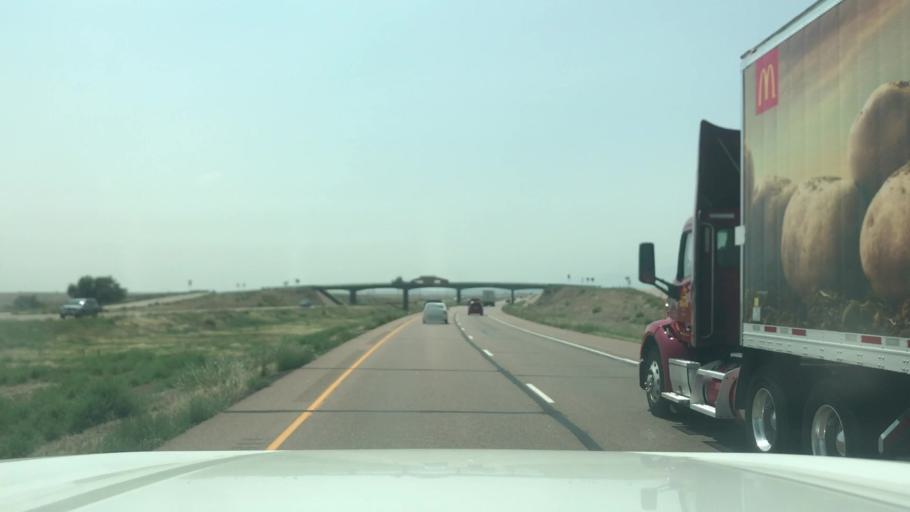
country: US
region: Colorado
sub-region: Pueblo County
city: Pueblo
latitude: 38.1632
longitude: -104.6421
